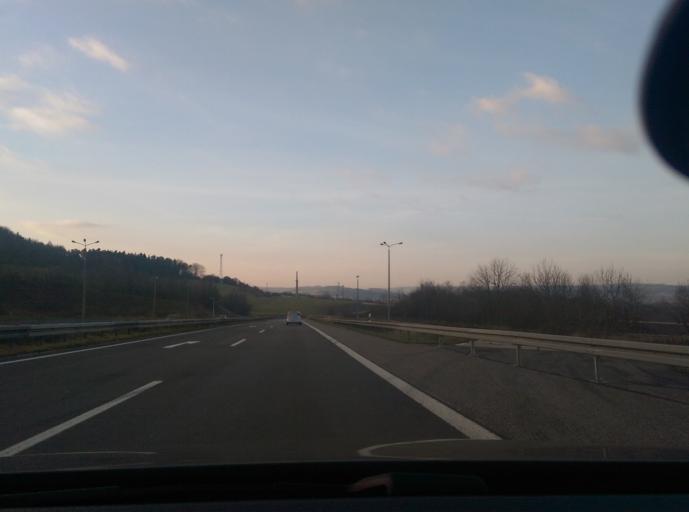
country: DE
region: Thuringia
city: Krauthausen
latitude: 51.0002
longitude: 10.2741
